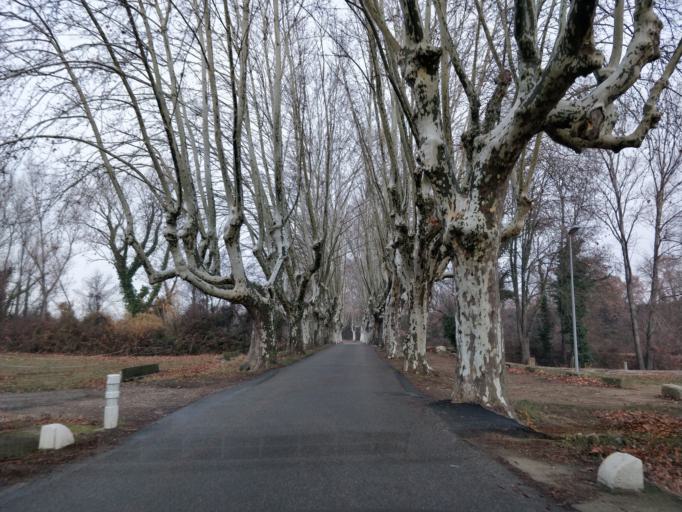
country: FR
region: Languedoc-Roussillon
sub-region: Departement du Gard
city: Saint-Mamert-du-Gard
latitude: 43.8986
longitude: 4.2120
